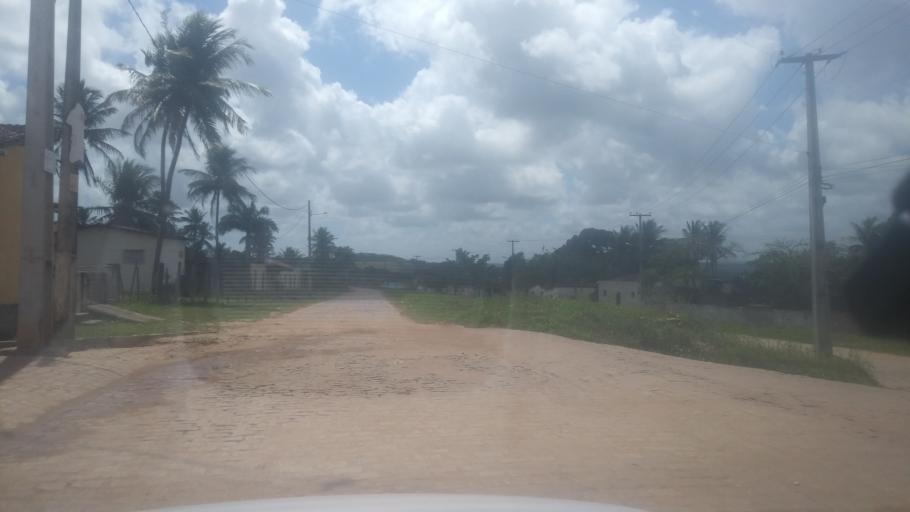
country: BR
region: Rio Grande do Norte
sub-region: Sao Jose De Mipibu
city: Sao Jose de Mipibu
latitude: -6.0700
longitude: -35.2351
